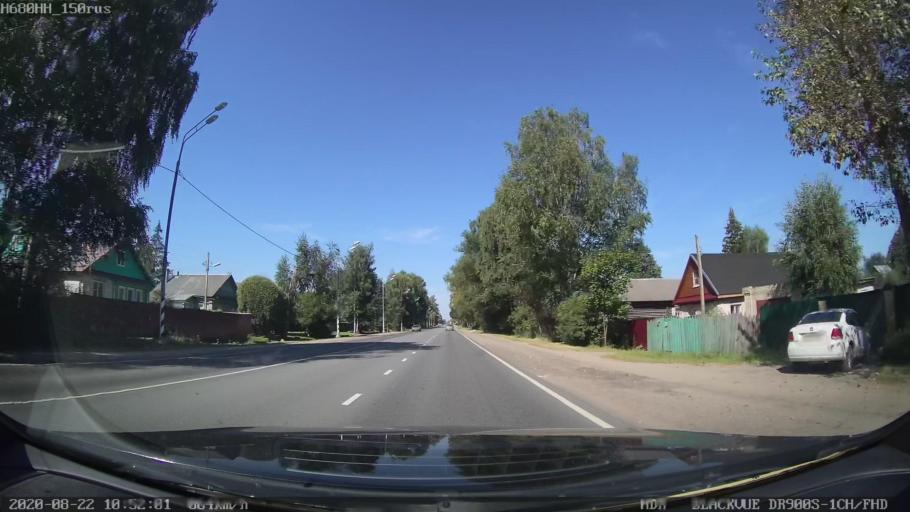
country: RU
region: Tverskaya
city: Emmaus
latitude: 56.7921
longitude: 36.0675
